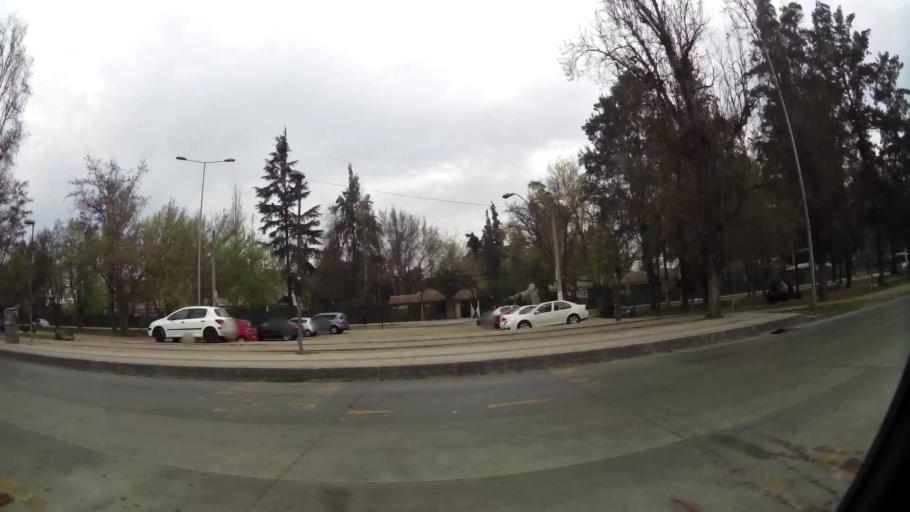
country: CL
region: Santiago Metropolitan
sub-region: Provincia de Santiago
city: Lo Prado
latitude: -33.5106
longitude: -70.7510
